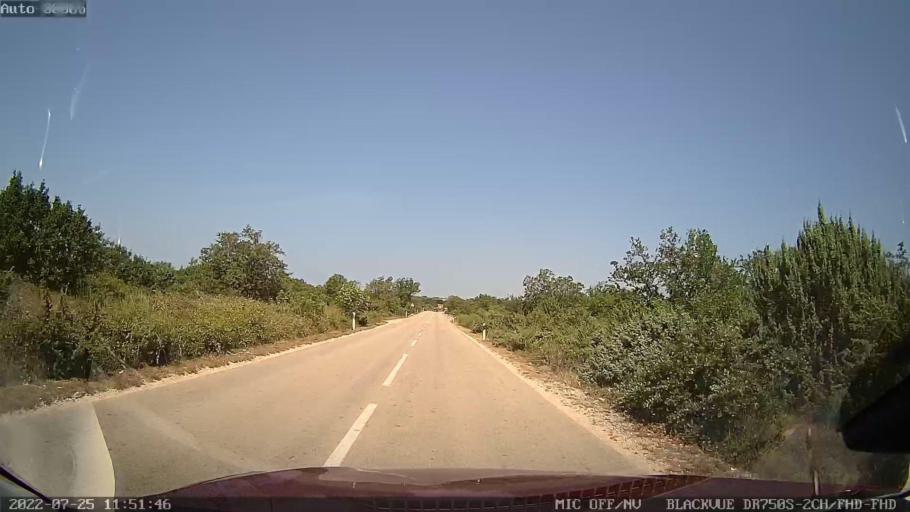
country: HR
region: Zadarska
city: Vrsi
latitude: 44.2419
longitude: 15.2495
